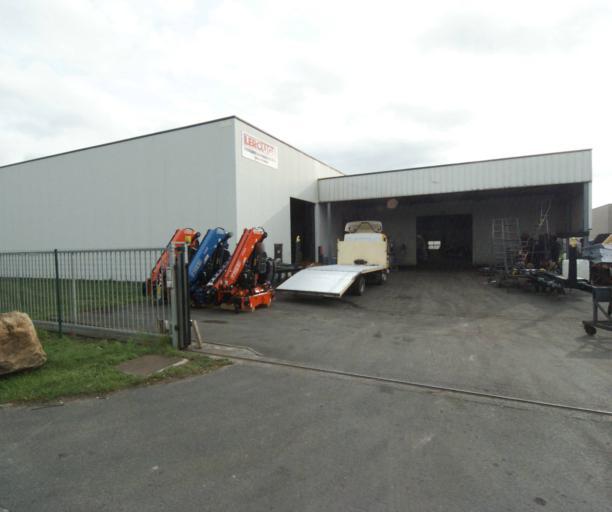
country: FR
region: Nord-Pas-de-Calais
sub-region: Departement du Nord
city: Bois-Grenier
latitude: 50.6569
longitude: 2.8941
